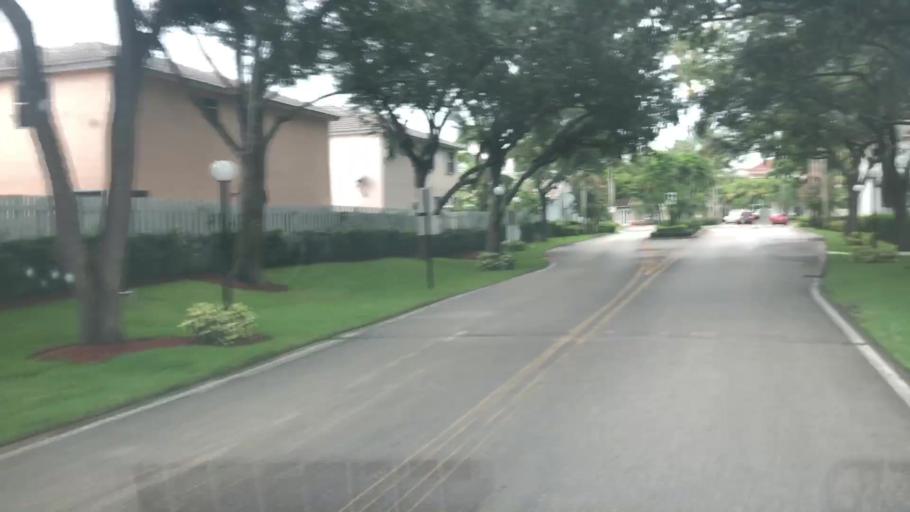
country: US
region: Florida
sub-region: Palm Beach County
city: Boca Pointe
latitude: 26.2995
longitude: -80.1828
